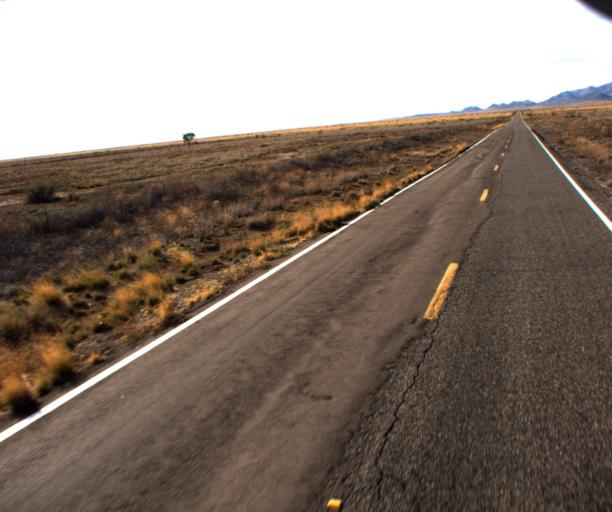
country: US
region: Arizona
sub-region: Cochise County
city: Willcox
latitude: 32.0702
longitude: -109.5110
